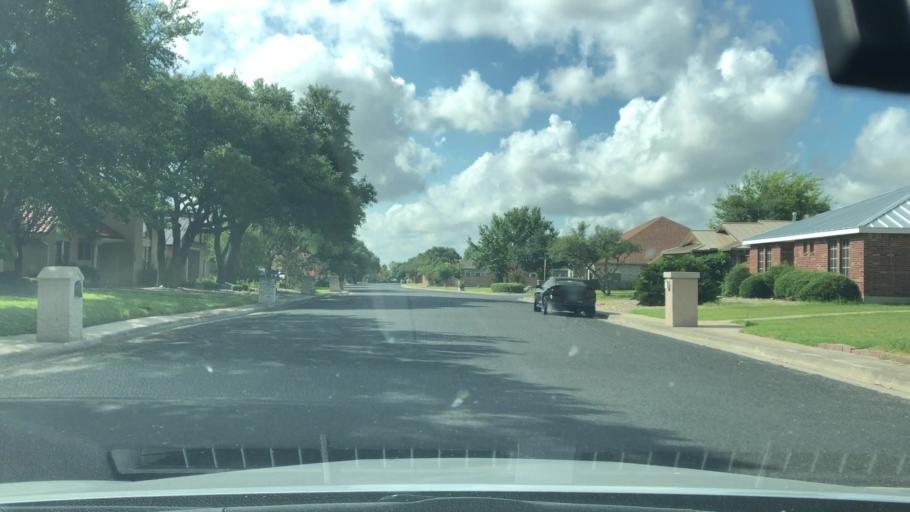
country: US
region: Texas
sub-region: Bexar County
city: Converse
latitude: 29.4879
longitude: -98.3373
